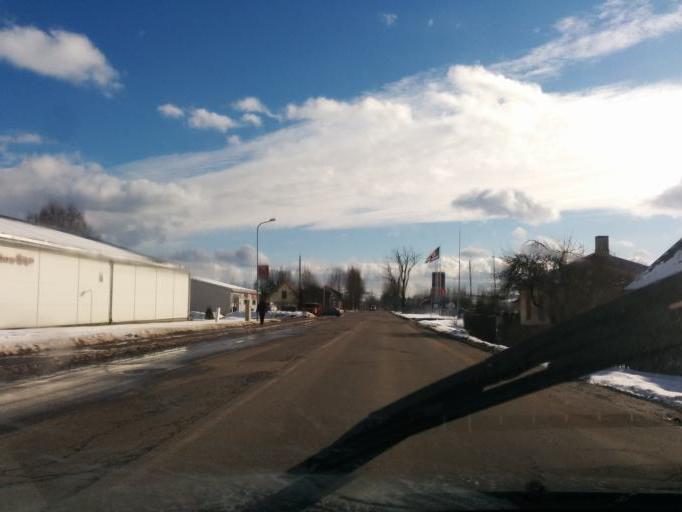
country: LV
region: Gulbenes Rajons
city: Gulbene
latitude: 57.1784
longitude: 26.7424
